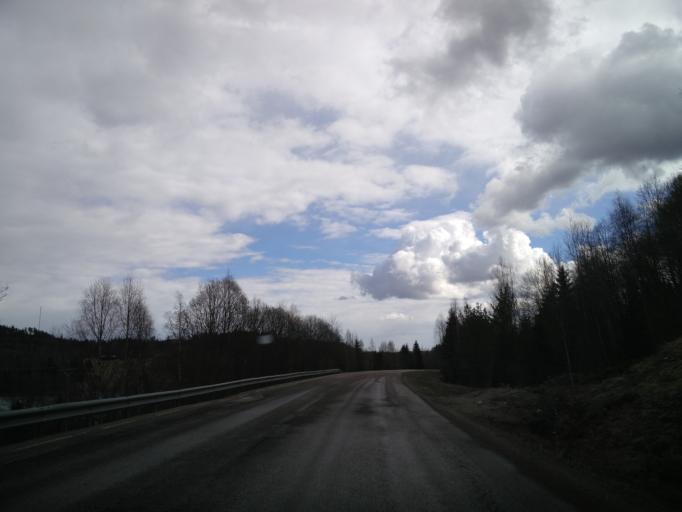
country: SE
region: Vaesternorrland
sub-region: Sundsvalls Kommun
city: Matfors
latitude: 62.4925
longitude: 17.1200
